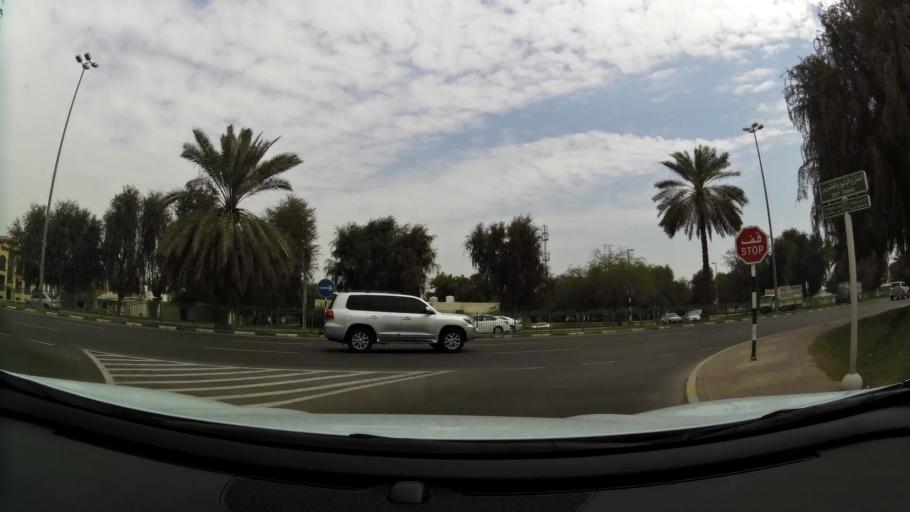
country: OM
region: Al Buraimi
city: Al Buraymi
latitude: 24.2278
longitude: 55.7841
